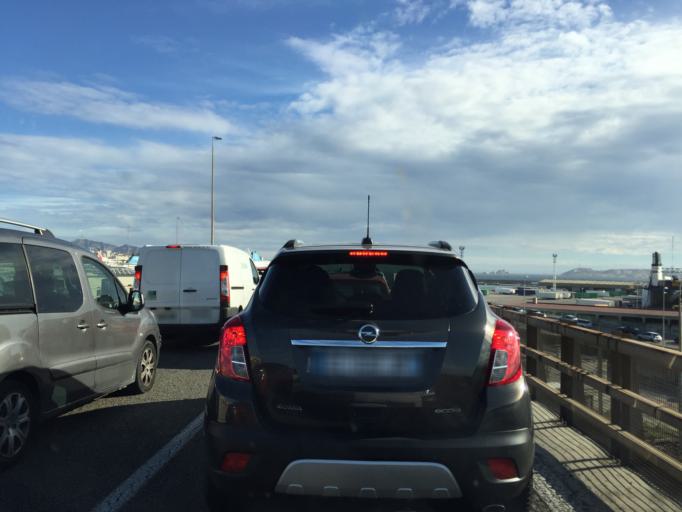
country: FR
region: Provence-Alpes-Cote d'Azur
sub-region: Departement des Bouches-du-Rhone
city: Marseille 03
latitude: 43.3198
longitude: 5.3636
